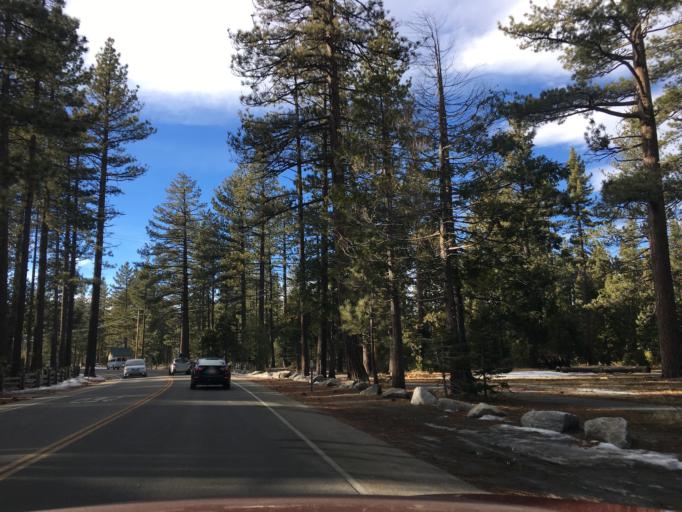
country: US
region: California
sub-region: El Dorado County
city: South Lake Tahoe
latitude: 38.9344
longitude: -120.0414
